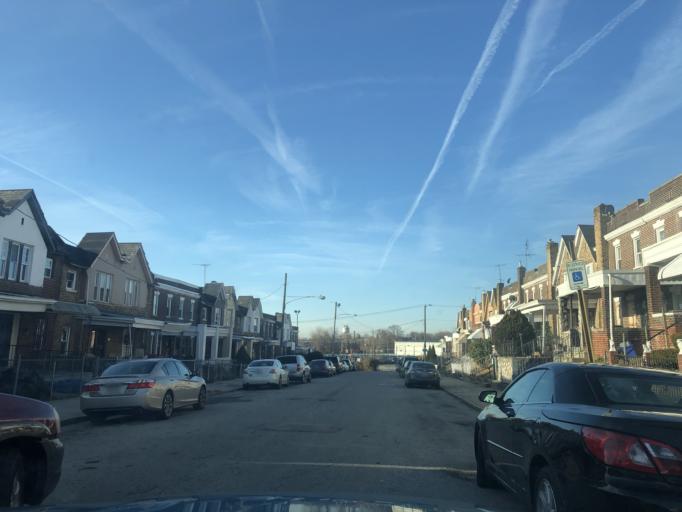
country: US
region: Pennsylvania
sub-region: Montgomery County
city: Bala-Cynwyd
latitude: 39.9821
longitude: -75.2289
